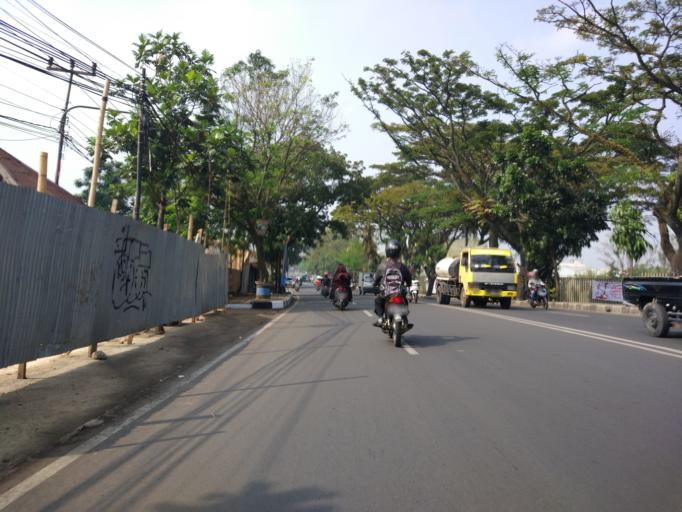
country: ID
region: West Java
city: Cileunyi
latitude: -6.9276
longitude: 107.7113
